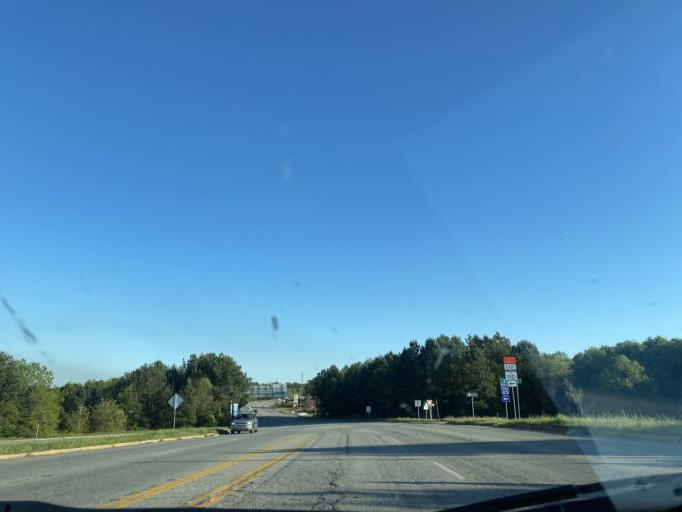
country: US
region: South Carolina
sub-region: Spartanburg County
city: Mayo
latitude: 35.0261
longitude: -81.8760
